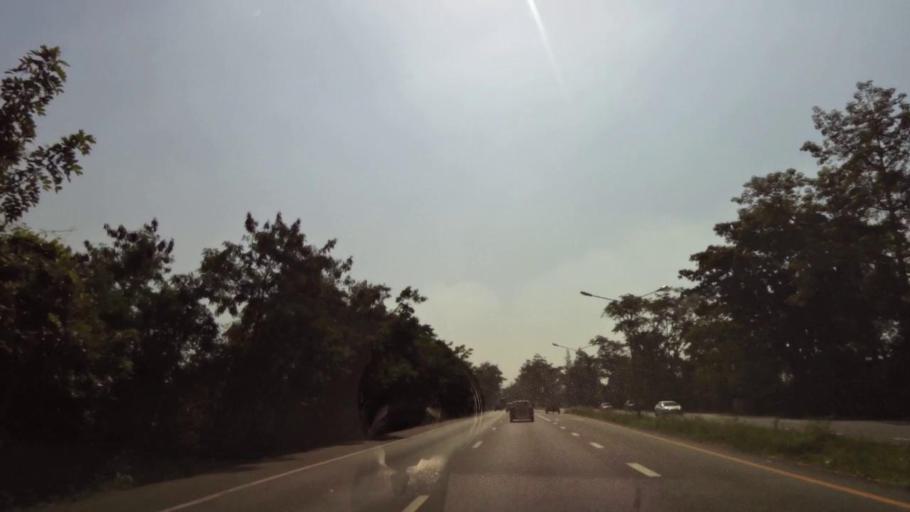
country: TH
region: Phichit
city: Bueng Na Rang
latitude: 16.0359
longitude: 100.1166
